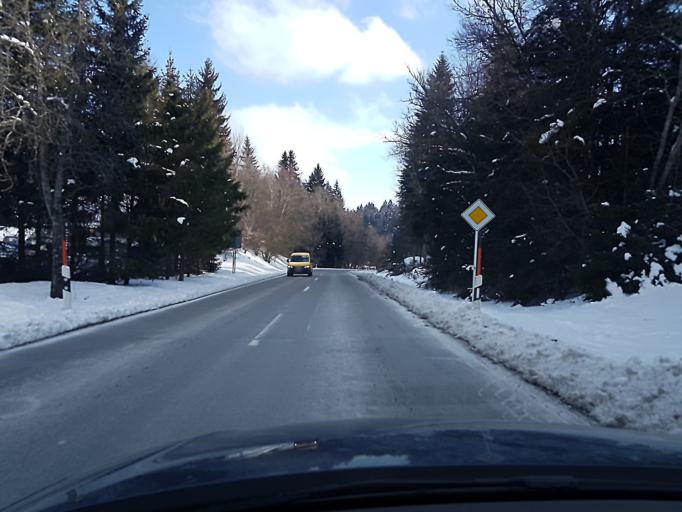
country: DE
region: Baden-Wuerttemberg
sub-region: Freiburg Region
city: Konigsfeld im Schwarzwald
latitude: 48.1415
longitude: 8.4286
